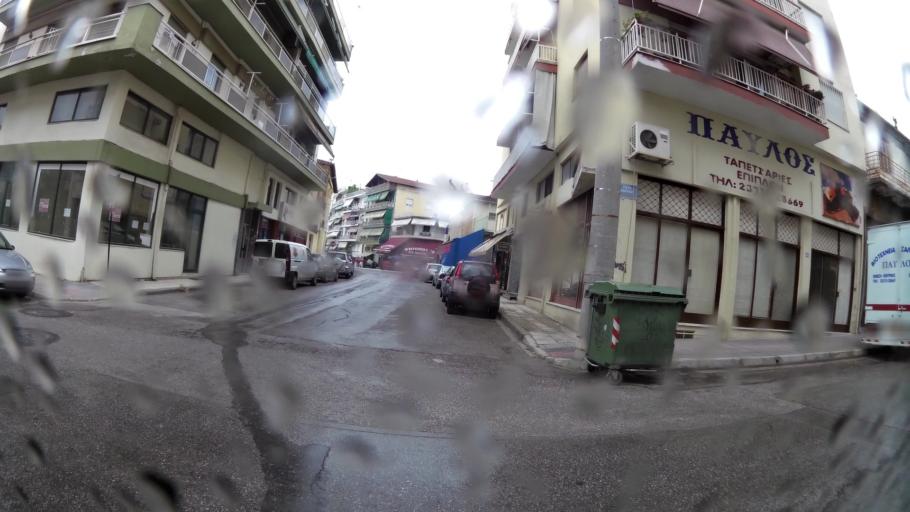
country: GR
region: Central Macedonia
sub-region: Nomos Imathias
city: Veroia
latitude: 40.5286
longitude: 22.2011
